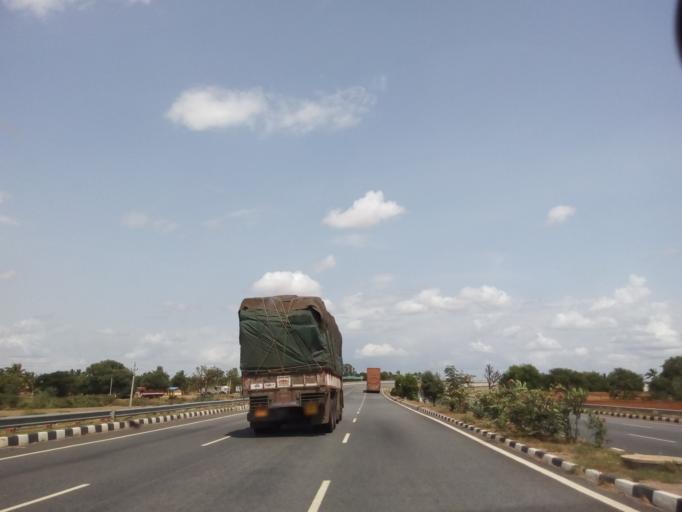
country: IN
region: Karnataka
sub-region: Tumkur
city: Sira
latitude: 13.7166
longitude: 76.9116
